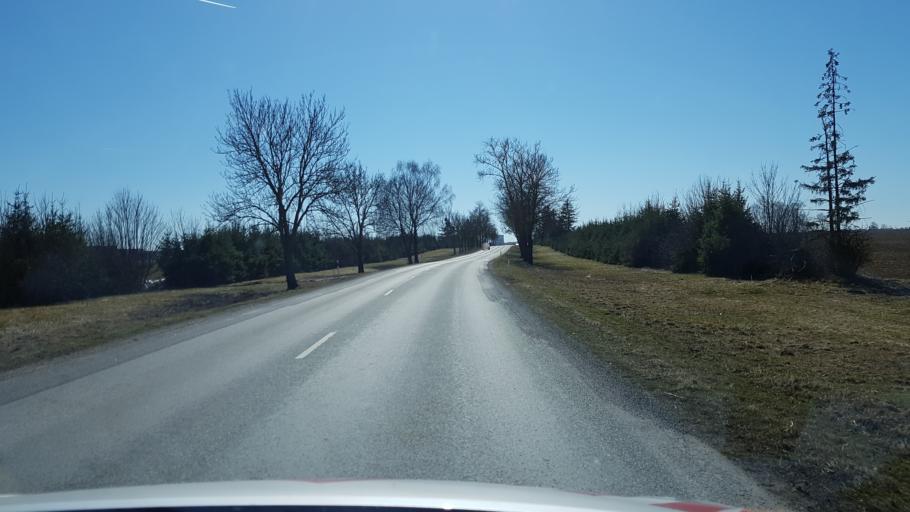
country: EE
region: Laeaene-Virumaa
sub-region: Rakvere linn
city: Rakvere
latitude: 59.3783
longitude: 26.3911
